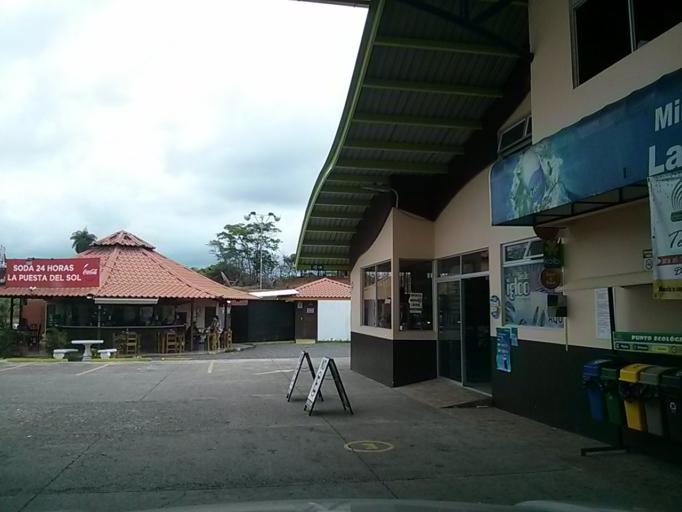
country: CR
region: Alajuela
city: Orotina
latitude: 9.8602
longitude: -84.5750
